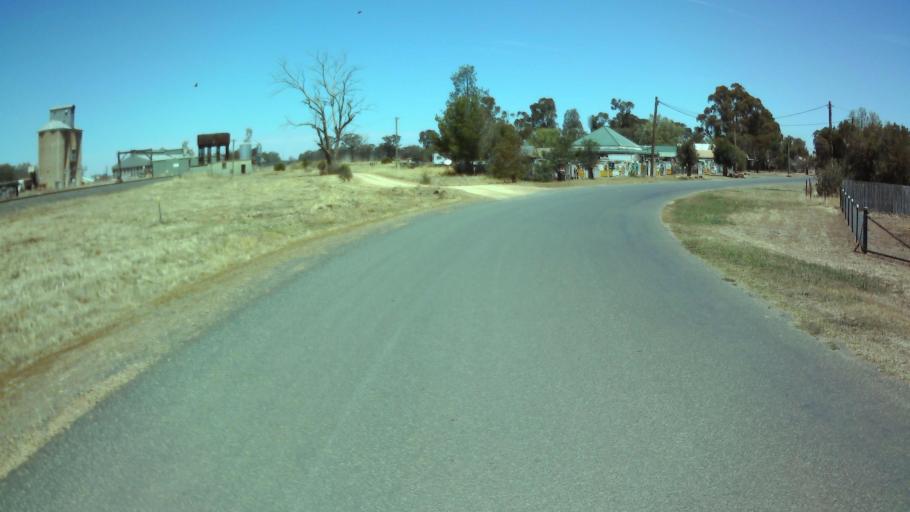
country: AU
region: New South Wales
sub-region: Weddin
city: Grenfell
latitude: -34.0106
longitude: 147.7944
